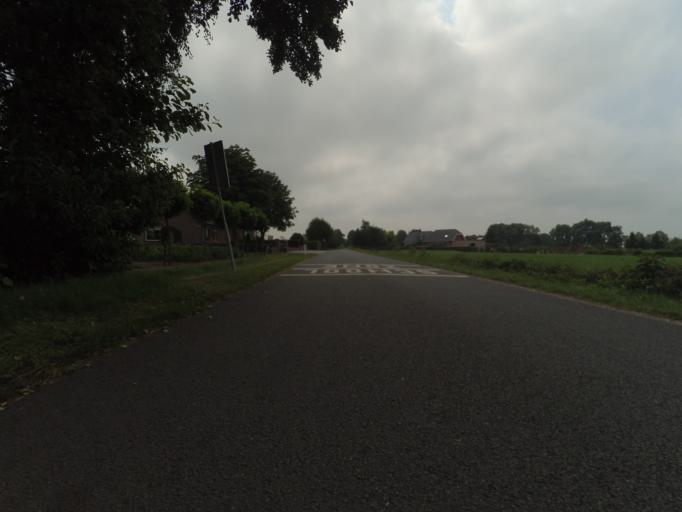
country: NL
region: Gelderland
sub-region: Gemeente Ede
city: Lunteren
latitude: 52.1229
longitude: 5.6355
